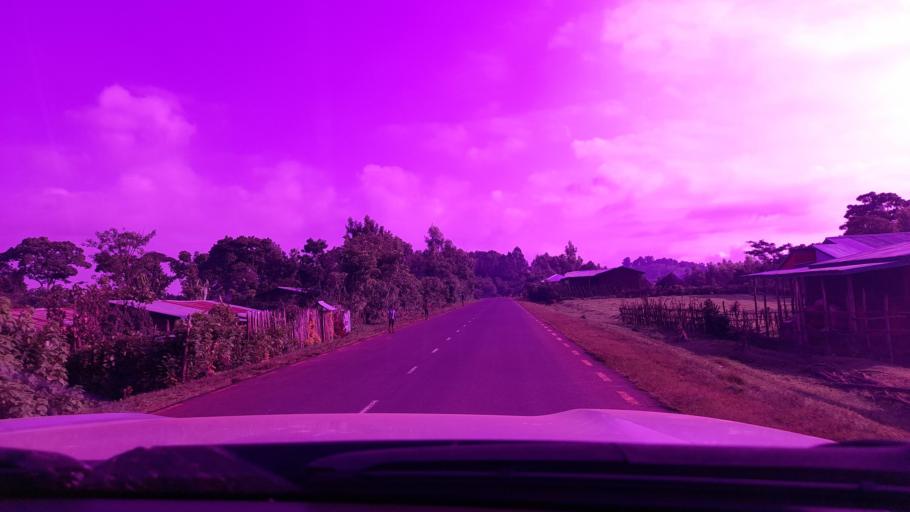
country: ET
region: Oromiya
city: Bedele
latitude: 8.1586
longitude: 36.4750
